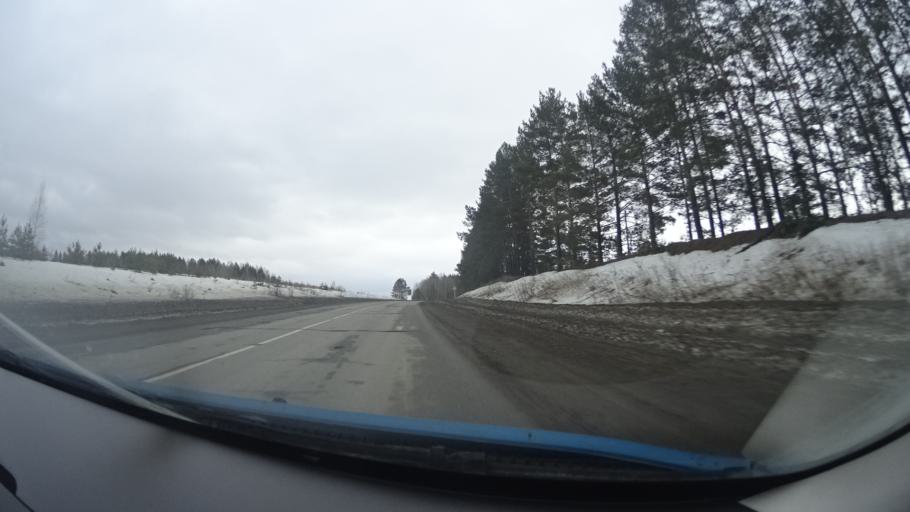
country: RU
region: Perm
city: Osa
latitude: 57.3246
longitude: 55.6091
